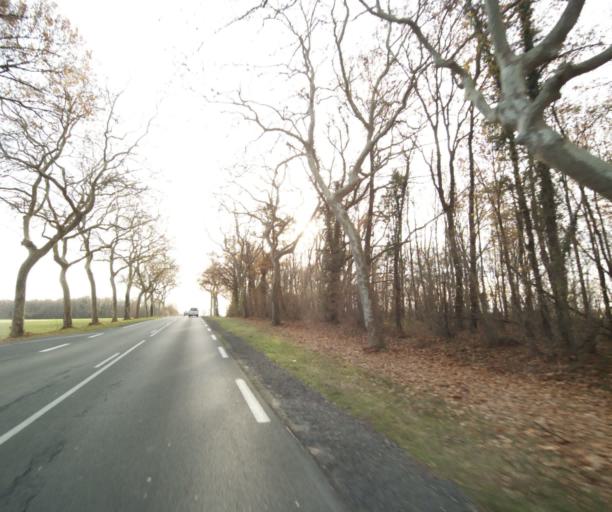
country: FR
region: Poitou-Charentes
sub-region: Departement de la Charente-Maritime
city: Saint-Hilaire-de-Villefranche
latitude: 45.8190
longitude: -0.5455
